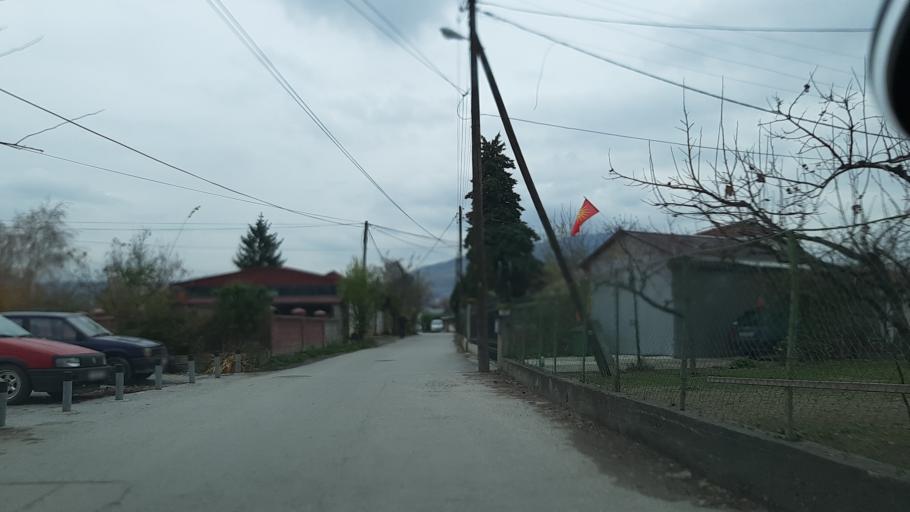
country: MK
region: Kisela Voda
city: Usje
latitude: 41.9766
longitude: 21.4746
